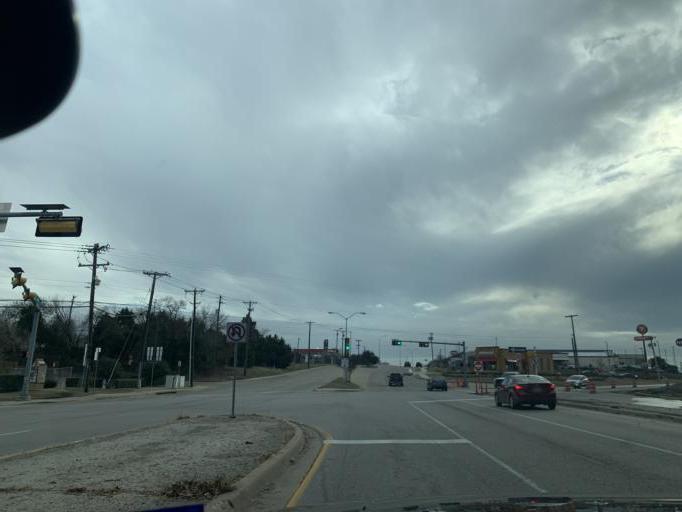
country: US
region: Texas
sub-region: Dallas County
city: Duncanville
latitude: 32.6248
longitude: -96.9084
